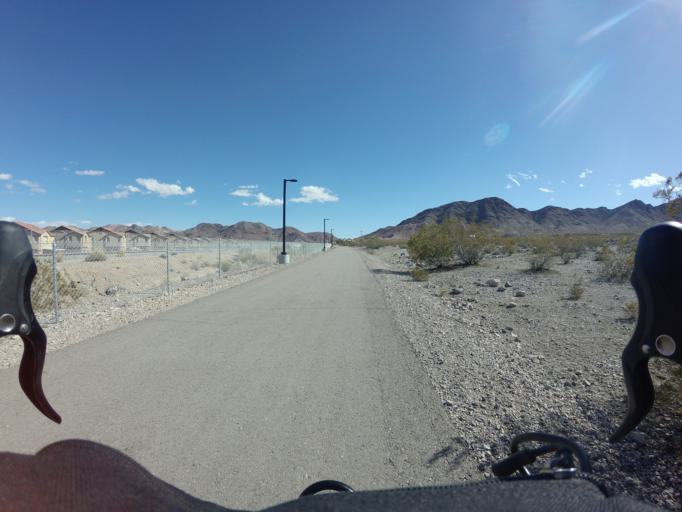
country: US
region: Nevada
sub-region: Clark County
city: Henderson
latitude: 35.9869
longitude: -114.9344
